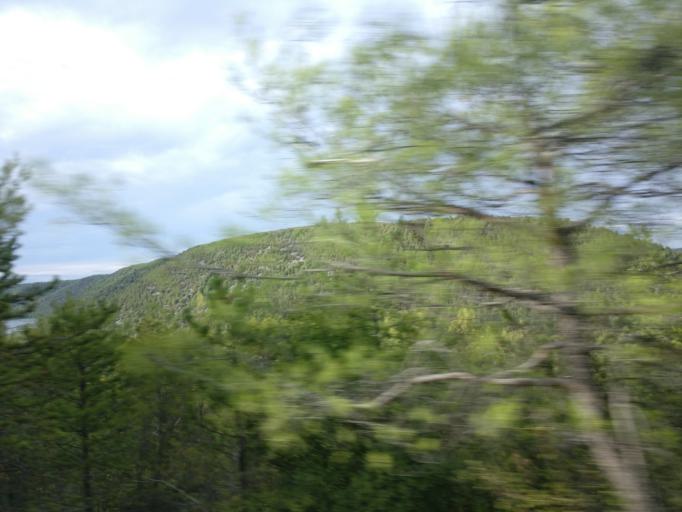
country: HR
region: Sibensko-Kniniska
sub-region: Grad Sibenik
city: Sibenik
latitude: 43.8009
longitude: 15.9675
